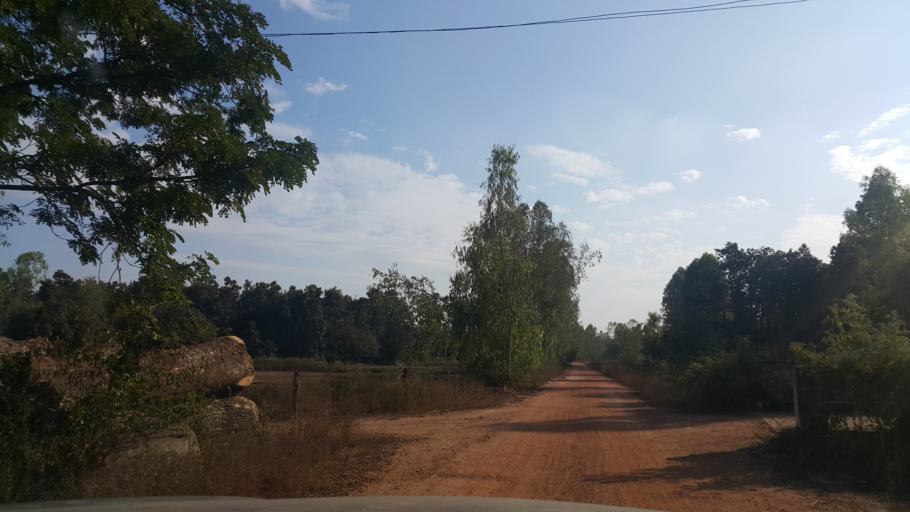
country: TH
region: Lampang
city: Hang Chat
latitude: 18.2665
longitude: 99.3719
